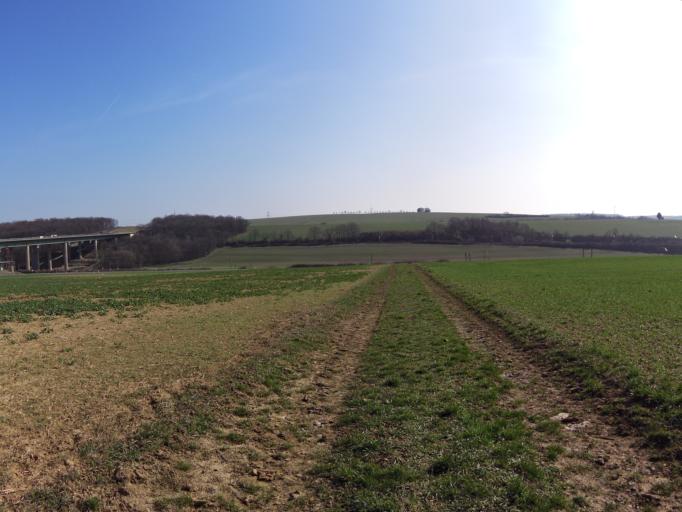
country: DE
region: Bavaria
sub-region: Regierungsbezirk Unterfranken
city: Rottendorf
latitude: 49.8048
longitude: 10.0418
